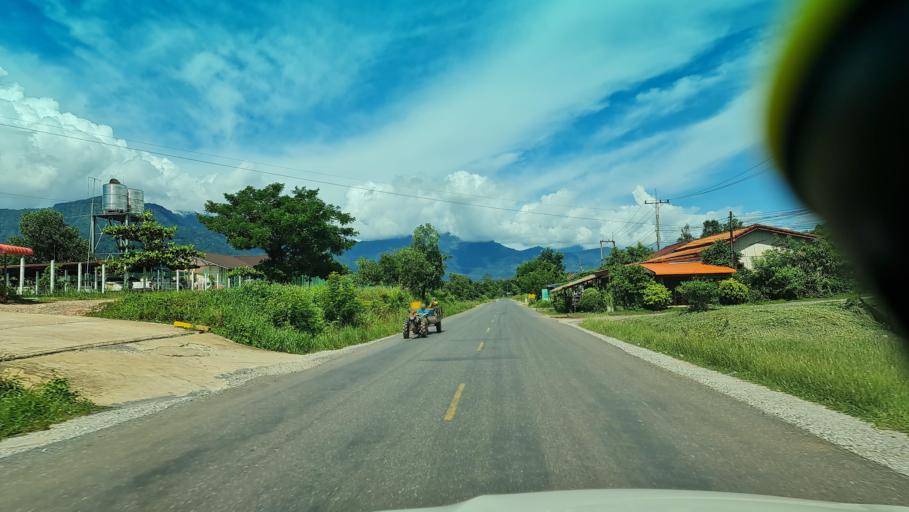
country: LA
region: Bolikhamxai
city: Ban Nahin
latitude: 18.3003
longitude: 104.1228
